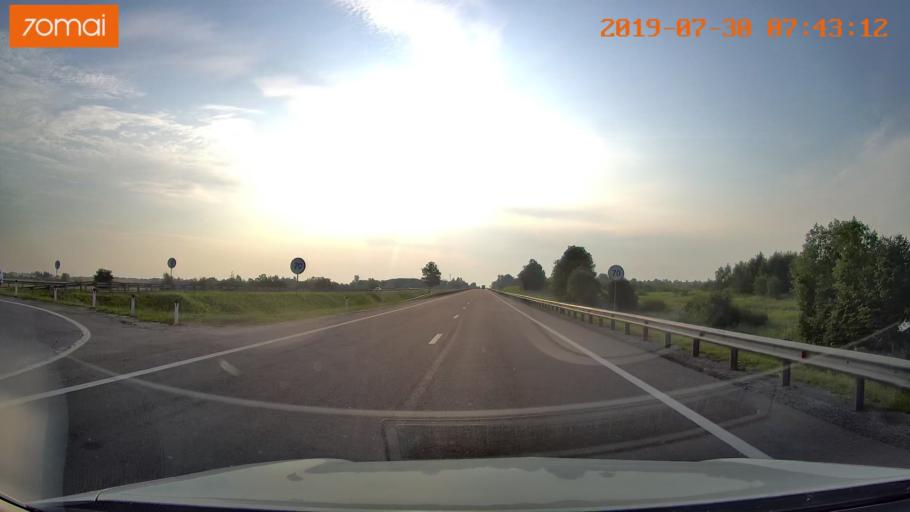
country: RU
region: Kaliningrad
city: Gvardeysk
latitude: 54.6487
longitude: 21.2996
